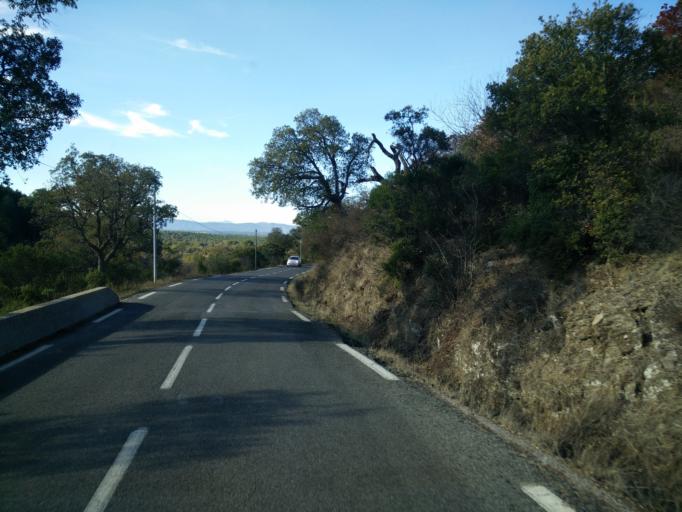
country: FR
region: Provence-Alpes-Cote d'Azur
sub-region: Departement du Var
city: La Garde-Freinet
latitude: 43.3321
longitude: 6.4361
